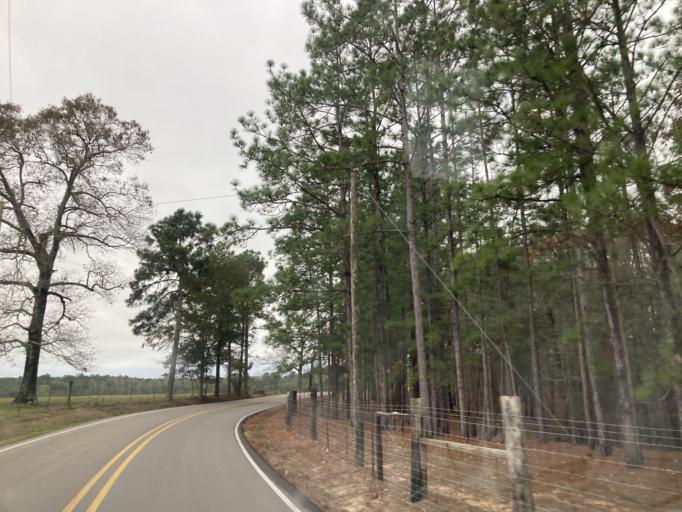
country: US
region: Mississippi
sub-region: Lamar County
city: Purvis
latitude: 31.1832
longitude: -89.4466
